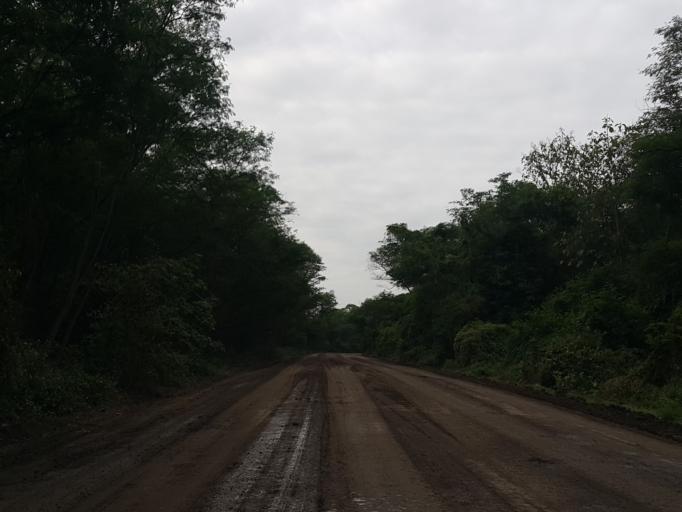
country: TH
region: Lampang
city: Mae Mo
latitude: 18.3135
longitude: 99.7496
